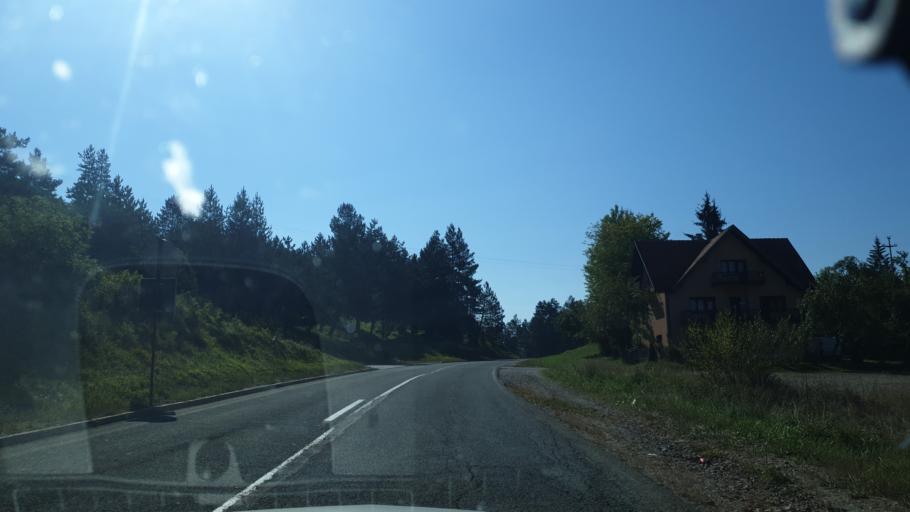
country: RS
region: Central Serbia
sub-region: Zlatiborski Okrug
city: Nova Varos
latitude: 43.5418
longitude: 19.7882
